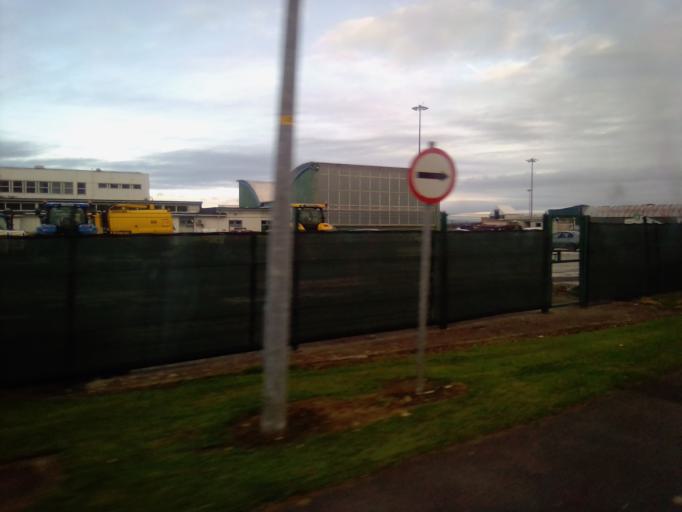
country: IE
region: Munster
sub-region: An Clar
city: Shannon
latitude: 52.6908
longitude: -8.9175
